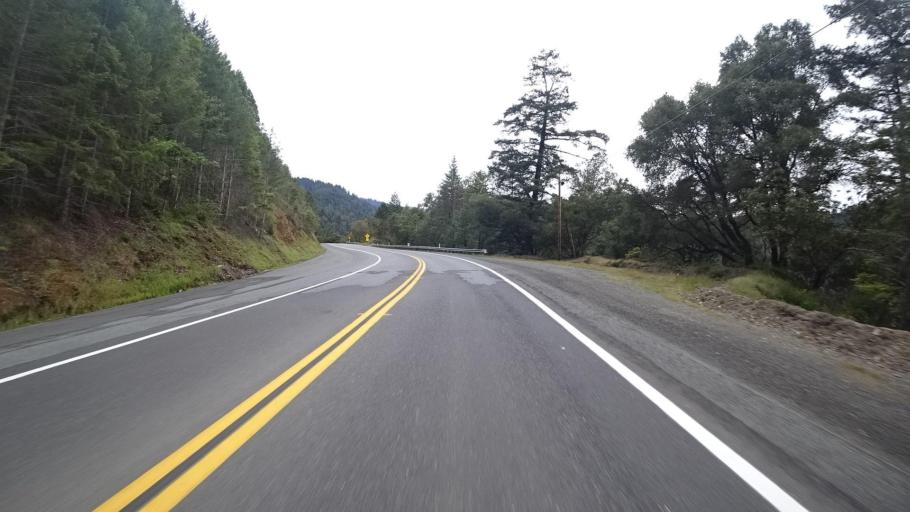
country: US
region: California
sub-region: Humboldt County
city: Willow Creek
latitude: 41.0004
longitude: -123.6345
